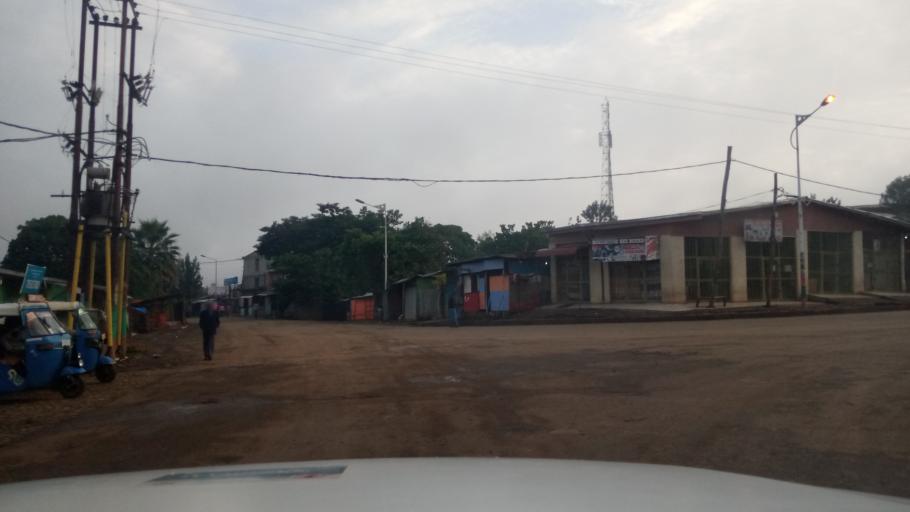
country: ET
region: Oromiya
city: Jima
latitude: 7.6834
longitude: 36.8498
